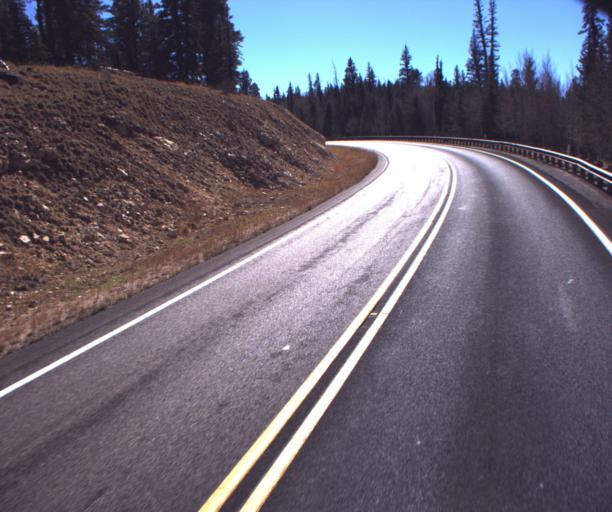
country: US
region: Arizona
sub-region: Coconino County
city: Grand Canyon
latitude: 36.5369
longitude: -112.1582
